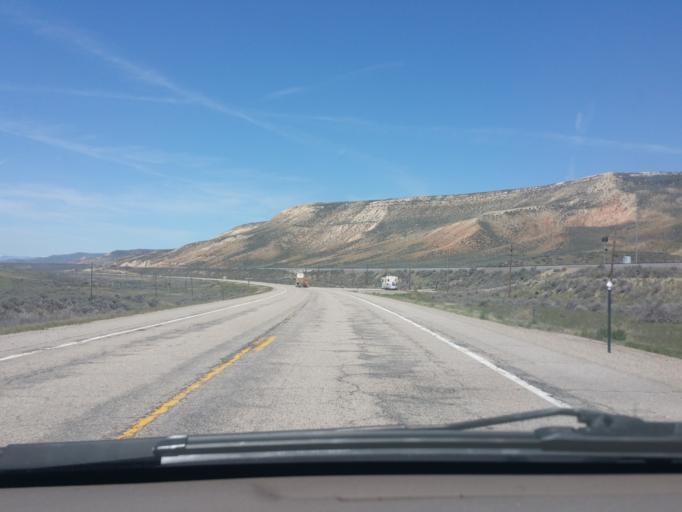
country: US
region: Wyoming
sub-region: Lincoln County
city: Kemmerer
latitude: 41.8143
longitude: -110.6277
